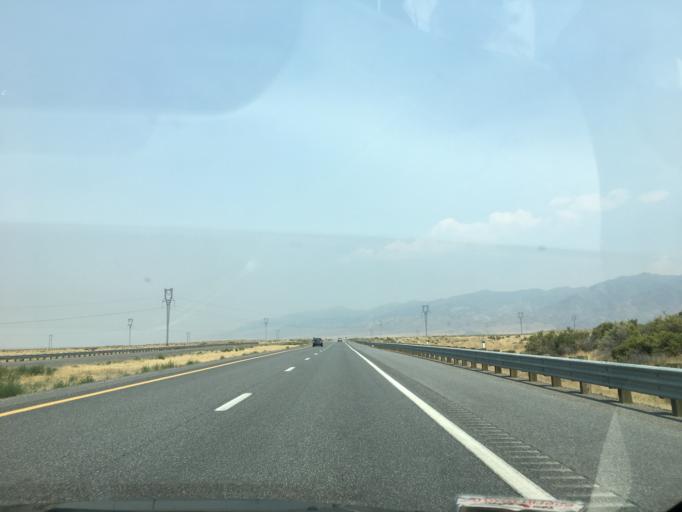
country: US
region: Nevada
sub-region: Pershing County
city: Lovelock
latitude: 40.3073
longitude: -118.3408
